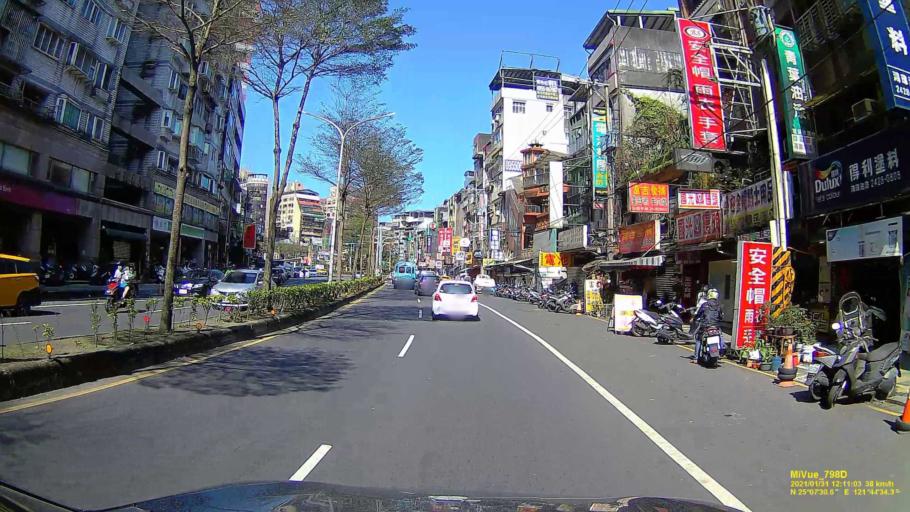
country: TW
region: Taiwan
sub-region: Keelung
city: Keelung
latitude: 25.1255
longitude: 121.7428
